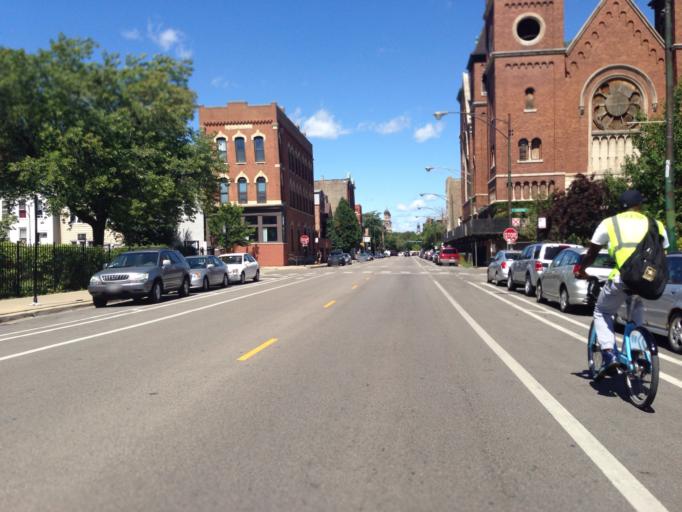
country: US
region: Illinois
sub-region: Cook County
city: Chicago
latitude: 41.8975
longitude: -87.6623
